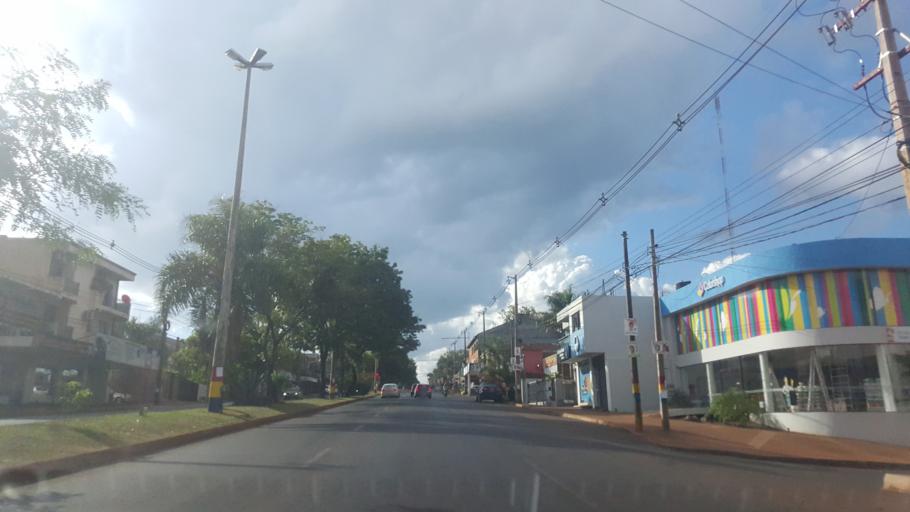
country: PY
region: Itapua
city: Encarnacion
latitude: -27.3322
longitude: -55.8587
